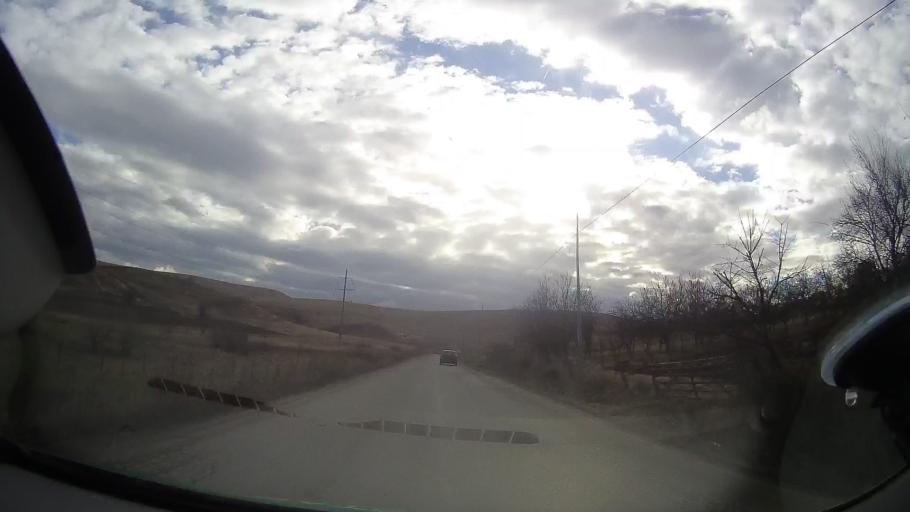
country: RO
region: Cluj
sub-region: Comuna Baisoara
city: Baisoara
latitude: 46.5998
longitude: 23.4629
